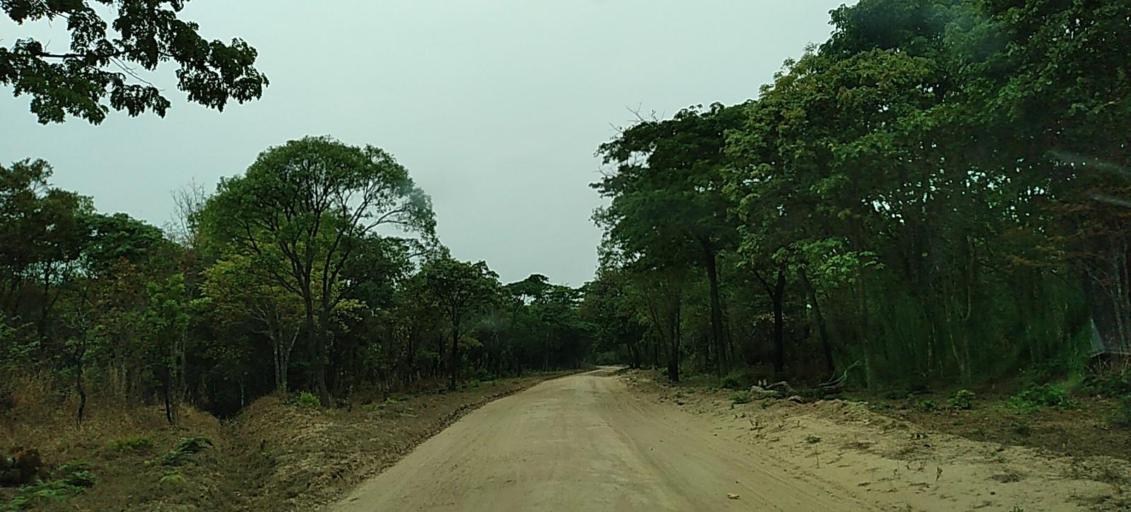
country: ZM
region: North-Western
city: Solwezi
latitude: -12.5316
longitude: 26.5231
